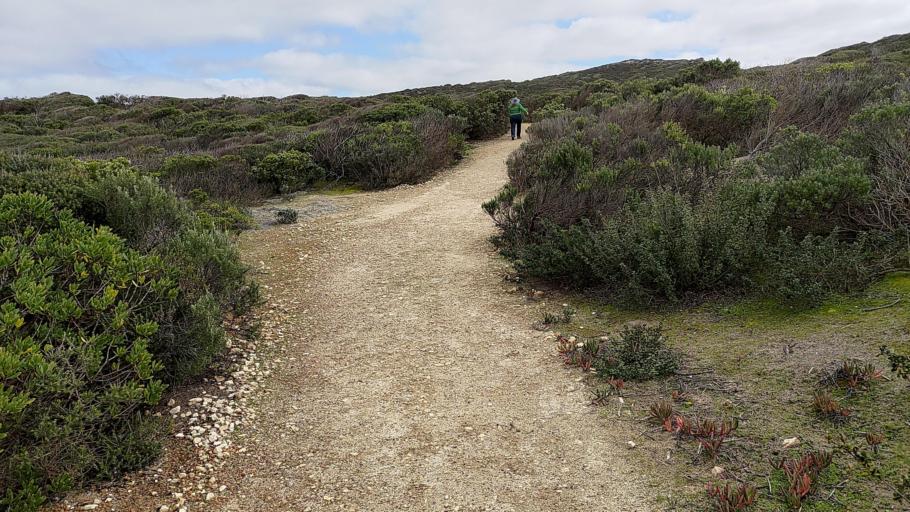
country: AU
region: South Australia
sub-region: Kangaroo Island
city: Kingscote
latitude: -35.9931
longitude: 137.3480
